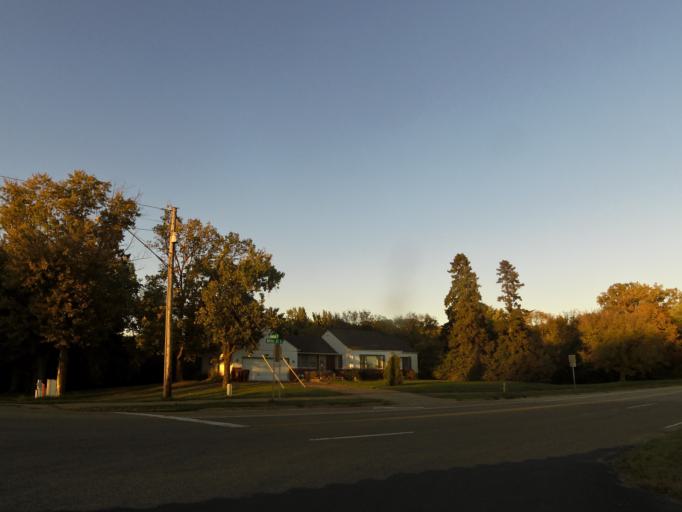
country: US
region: Minnesota
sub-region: Dakota County
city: Inver Grove Heights
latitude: 44.8332
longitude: -93.0671
